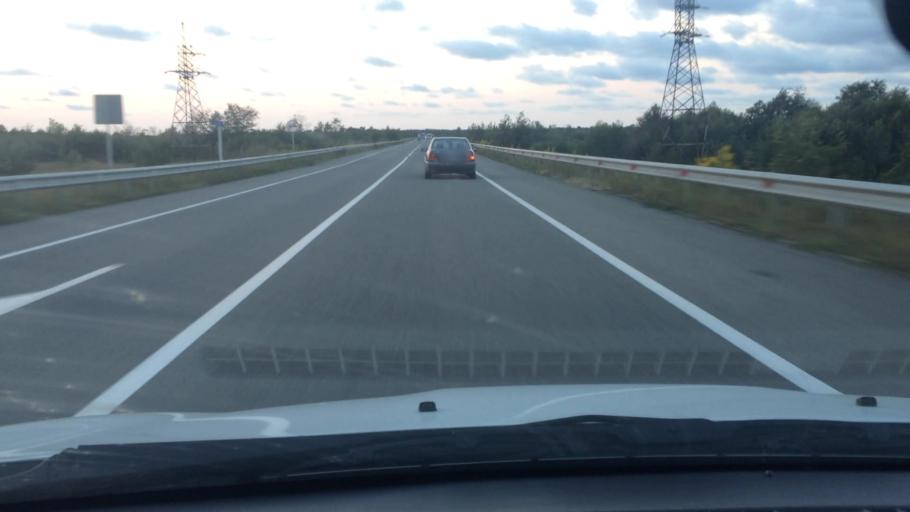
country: GE
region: Ajaria
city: Ochkhamuri
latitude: 41.9039
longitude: 41.7907
